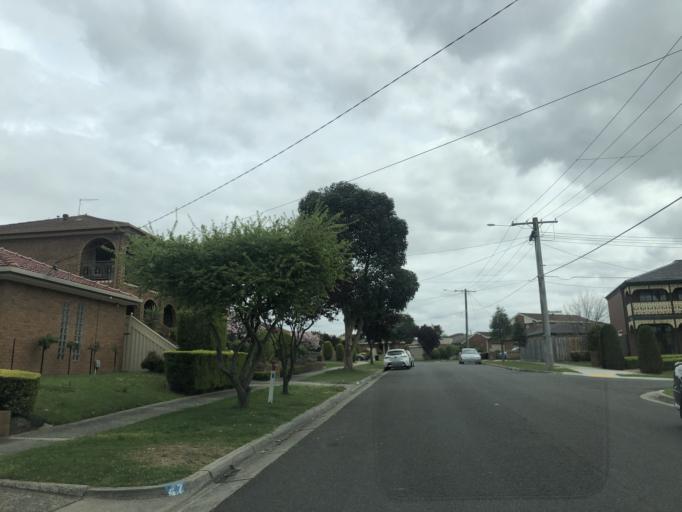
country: AU
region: Victoria
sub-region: Greater Dandenong
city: Dandenong North
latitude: -37.9519
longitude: 145.2188
